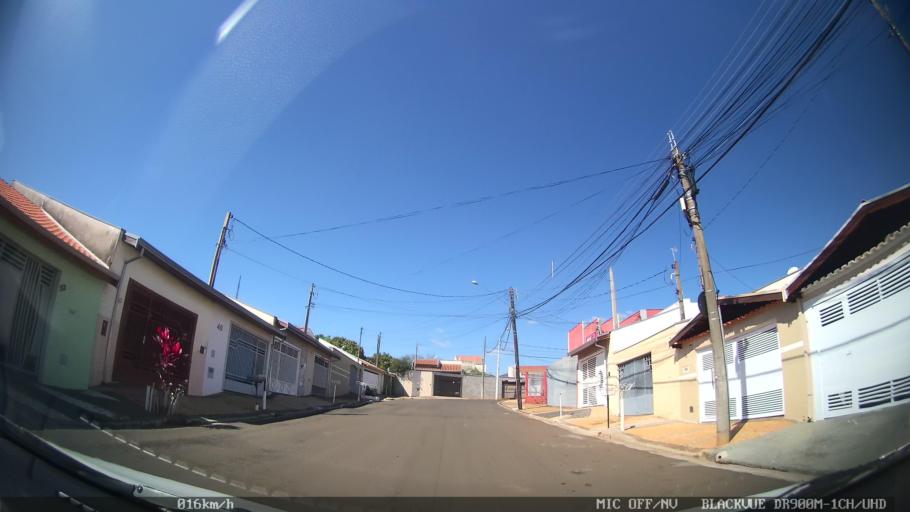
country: BR
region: Sao Paulo
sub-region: Santa Barbara D'Oeste
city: Santa Barbara d'Oeste
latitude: -22.7434
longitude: -47.4104
